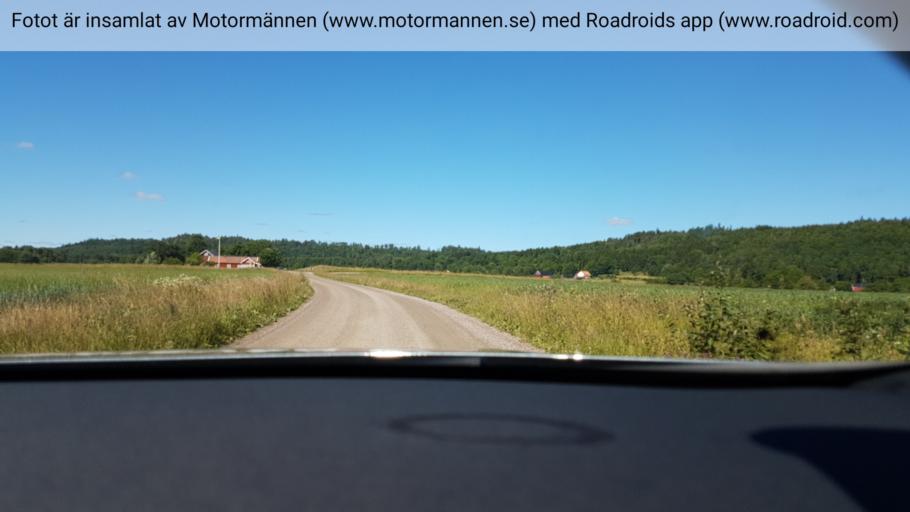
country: SE
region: Vaestra Goetaland
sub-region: Skovde Kommun
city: Skultorp
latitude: 58.2249
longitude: 13.7870
